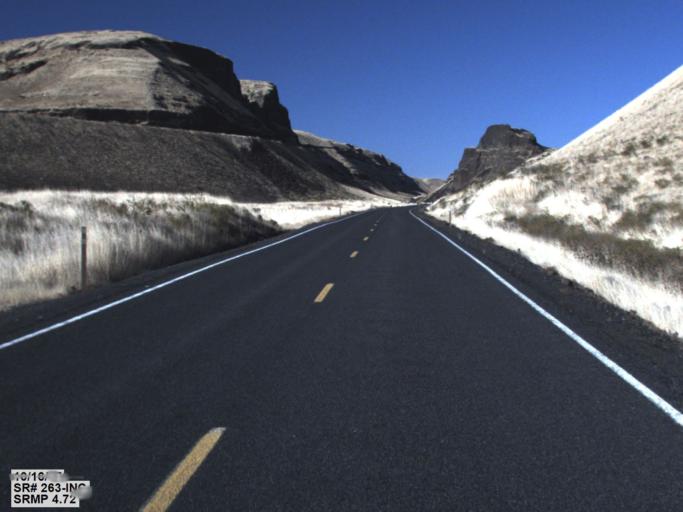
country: US
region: Washington
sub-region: Franklin County
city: Connell
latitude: 46.5835
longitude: -118.5411
